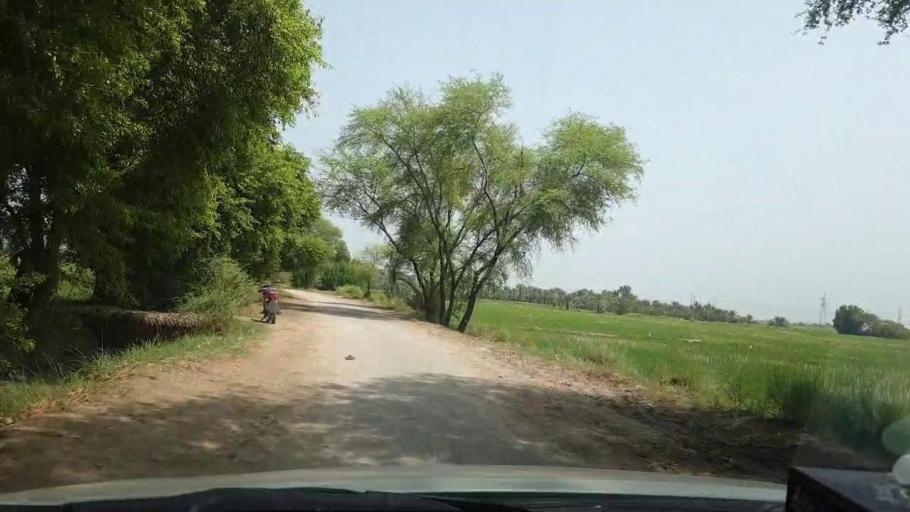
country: PK
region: Sindh
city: Shikarpur
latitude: 27.9870
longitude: 68.6982
